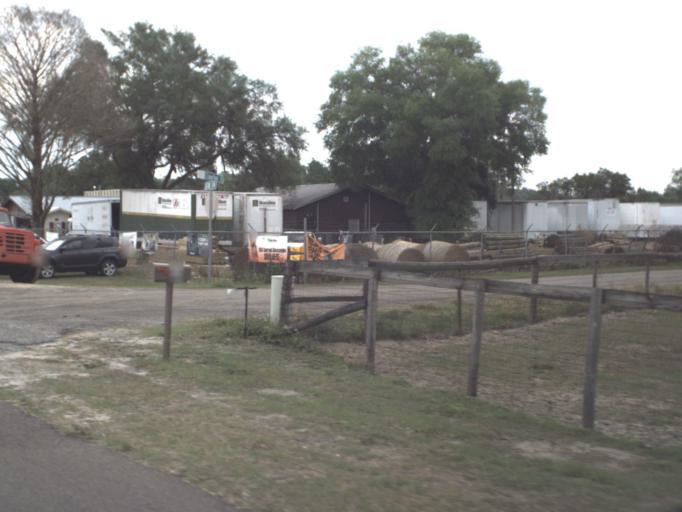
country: US
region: Florida
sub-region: Lake County
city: Umatilla
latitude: 28.9784
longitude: -81.6452
